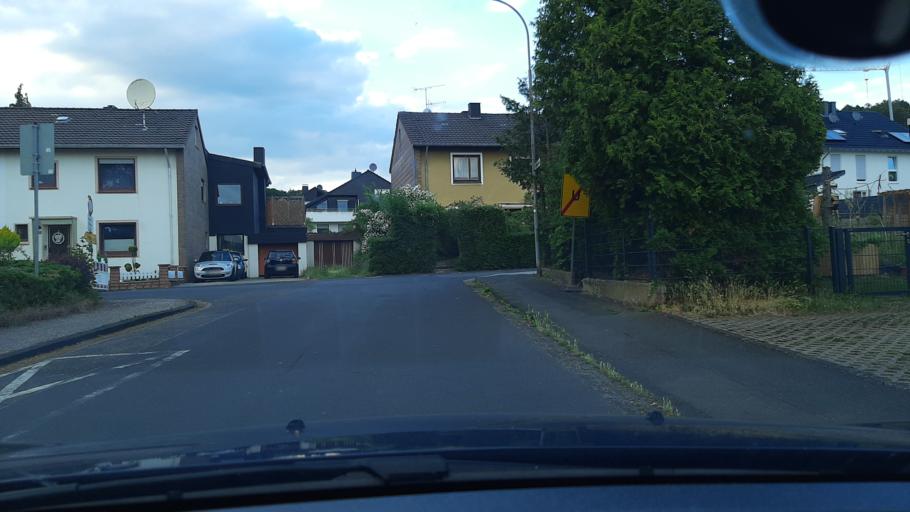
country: DE
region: North Rhine-Westphalia
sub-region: Regierungsbezirk Koln
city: Mechernich
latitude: 50.5939
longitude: 6.6492
